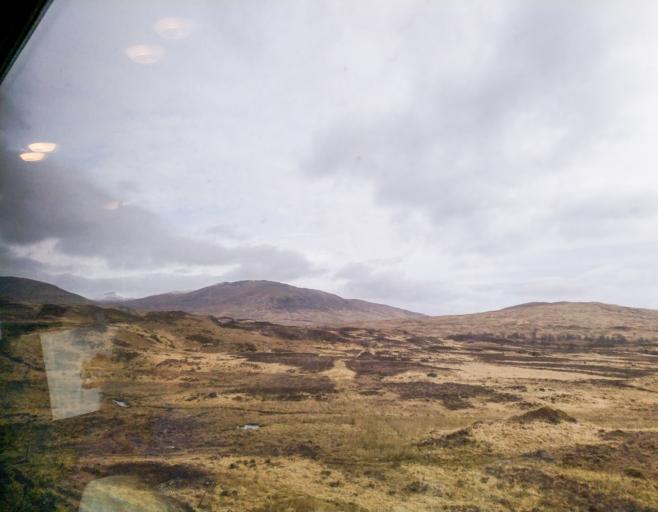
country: GB
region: Scotland
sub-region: Highland
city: Spean Bridge
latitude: 56.6888
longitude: -4.5765
